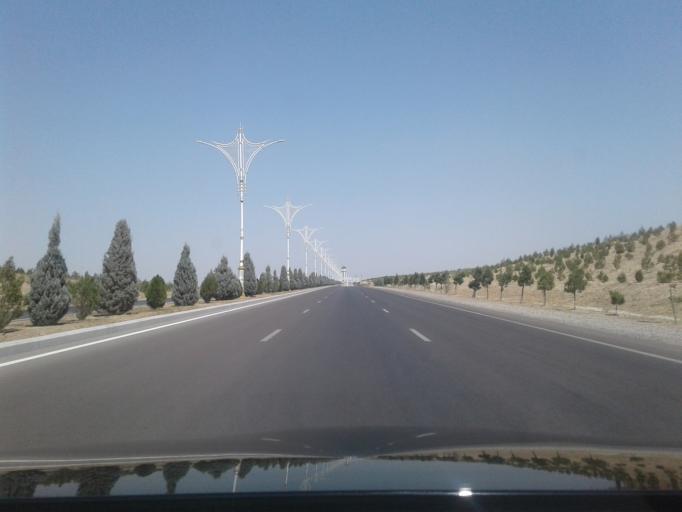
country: TM
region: Ahal
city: Ashgabat
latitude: 37.8784
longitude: 58.4080
